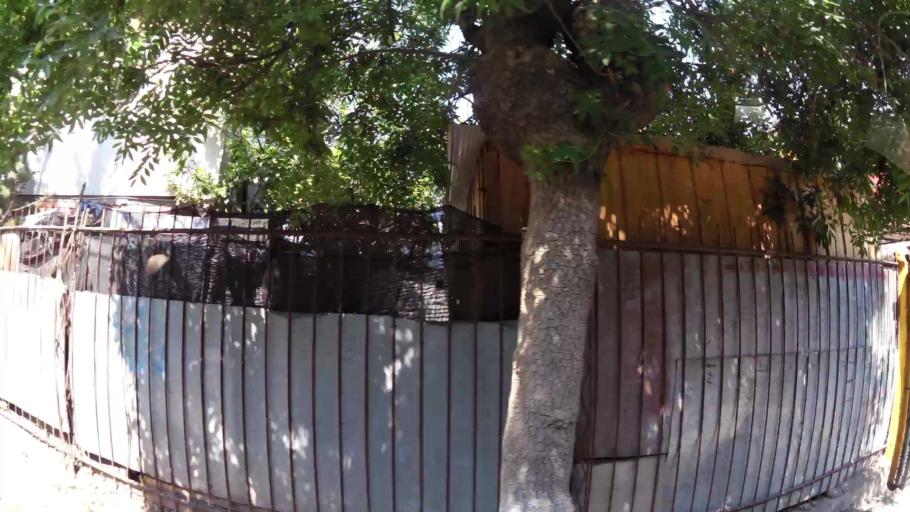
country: CL
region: Santiago Metropolitan
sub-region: Provincia de Santiago
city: La Pintana
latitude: -33.5518
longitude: -70.6063
